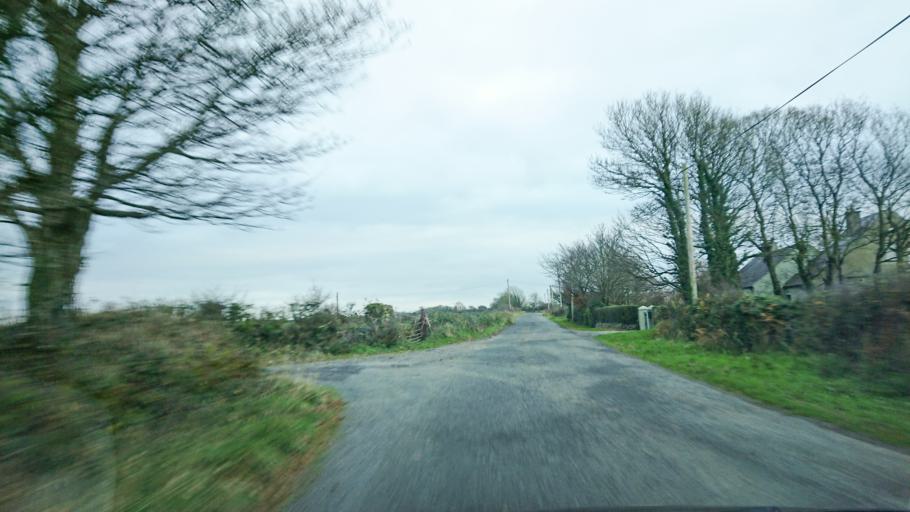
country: IE
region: Munster
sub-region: Waterford
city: Dunmore East
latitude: 52.2412
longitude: -6.9955
